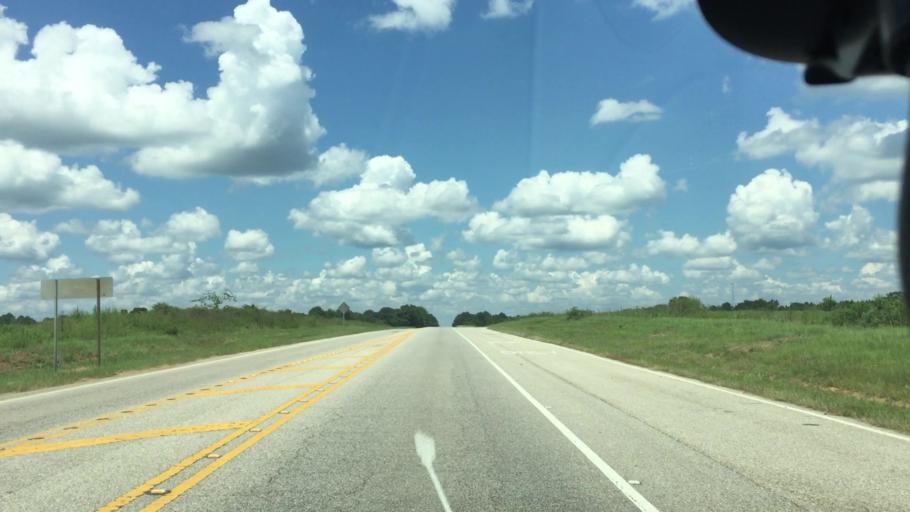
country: US
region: Alabama
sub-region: Coffee County
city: New Brockton
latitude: 31.4172
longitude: -85.8855
